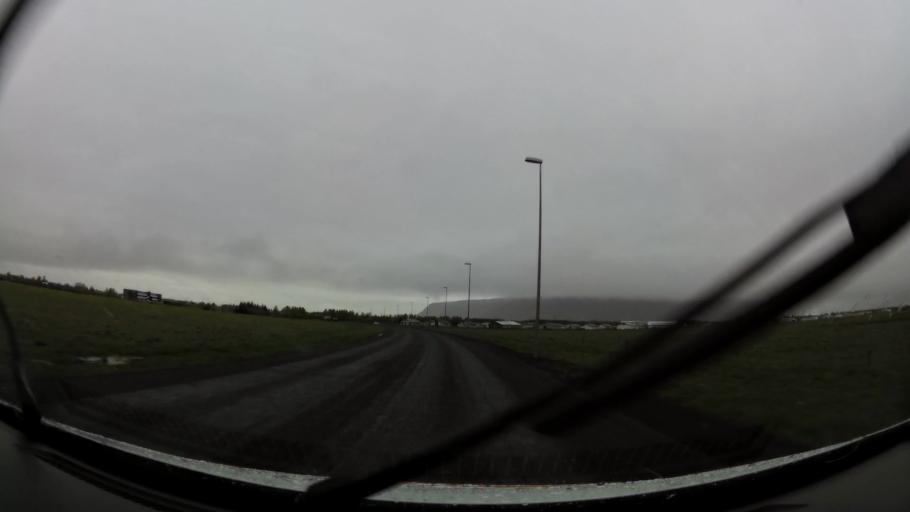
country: IS
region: South
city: Selfoss
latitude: 63.9296
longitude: -20.9719
